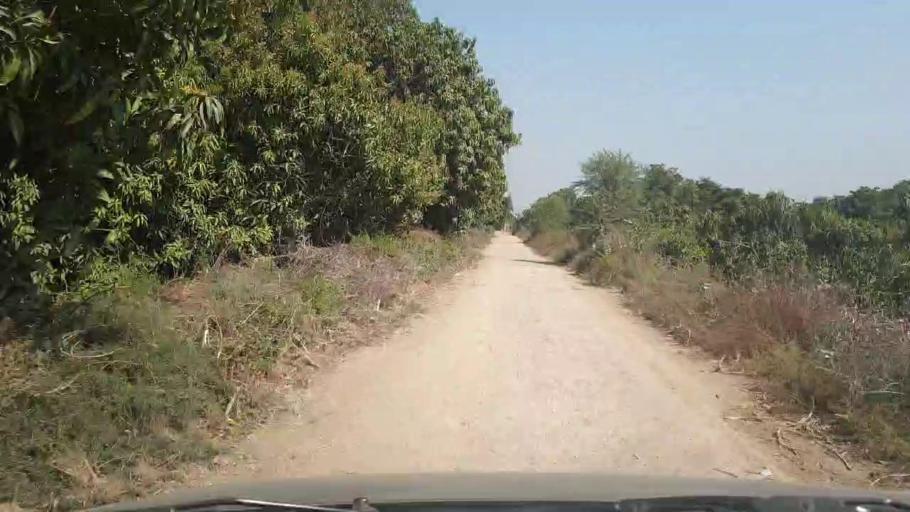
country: PK
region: Sindh
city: Mirwah Gorchani
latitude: 25.2548
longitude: 69.1268
